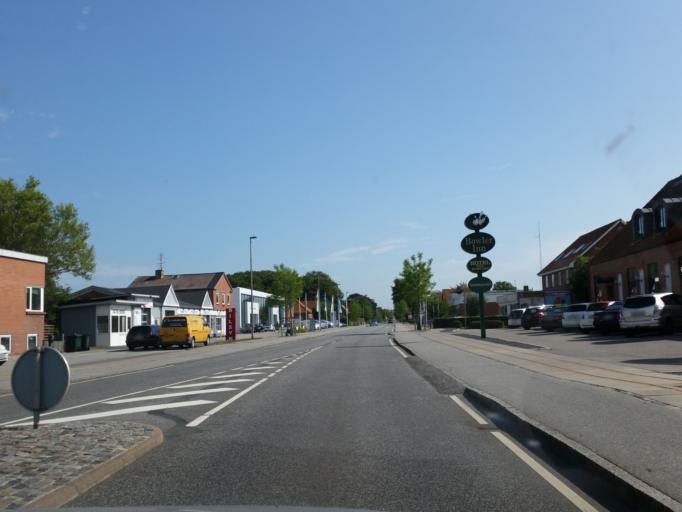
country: DK
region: South Denmark
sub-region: Tonder Kommune
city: Tonder
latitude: 54.9469
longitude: 8.8720
